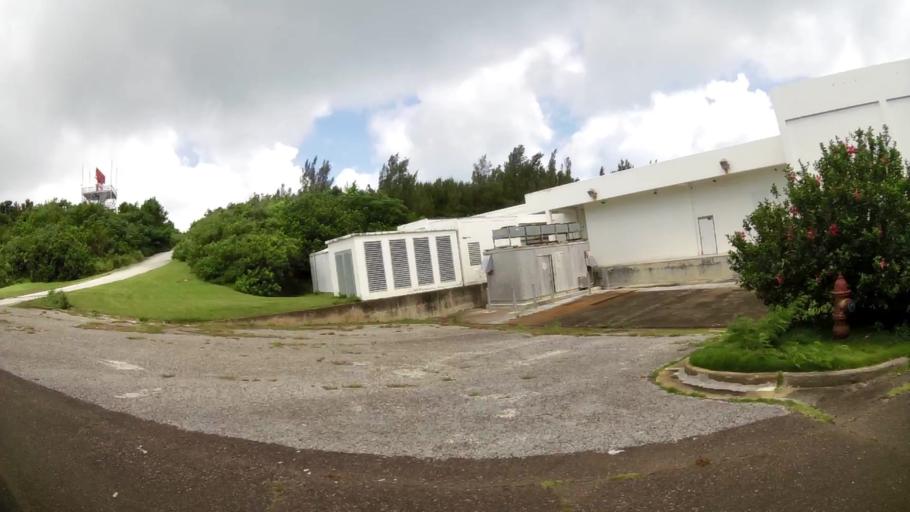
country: BM
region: Saint George
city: Saint George
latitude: 32.3675
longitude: -64.6763
